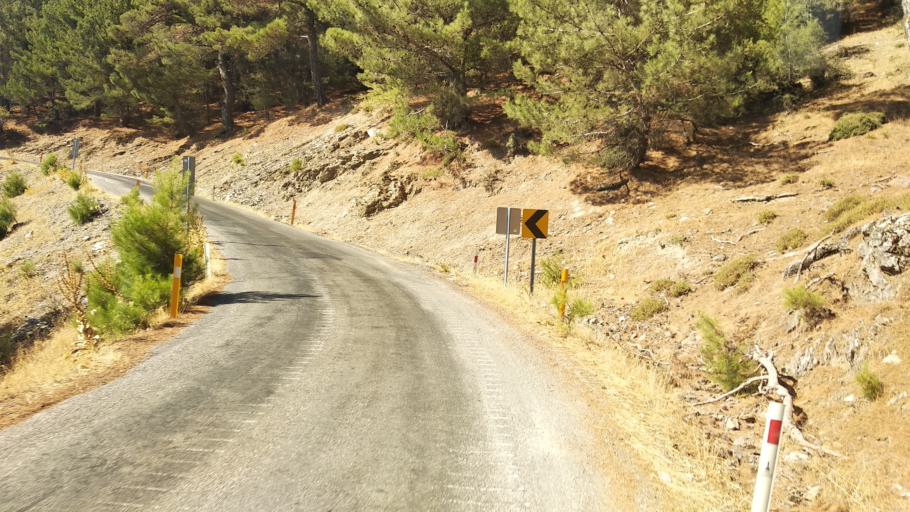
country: TR
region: Izmir
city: Gaziemir
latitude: 38.2964
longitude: 26.9995
